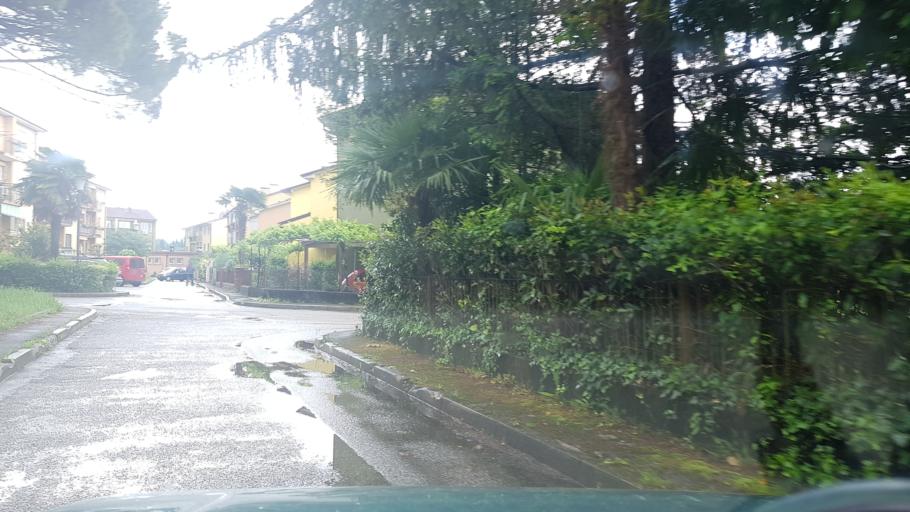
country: IT
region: Friuli Venezia Giulia
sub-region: Provincia di Gorizia
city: Gorizia
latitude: 45.9563
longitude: 13.6098
